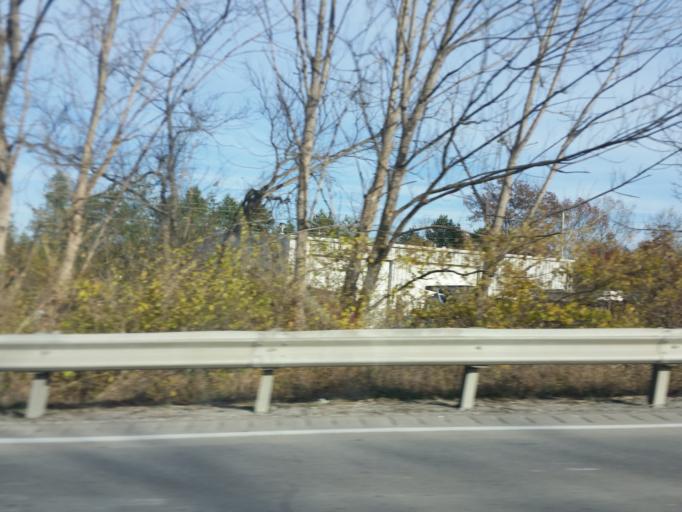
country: US
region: Kentucky
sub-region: Campbell County
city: Claryville
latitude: 38.8330
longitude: -84.3659
